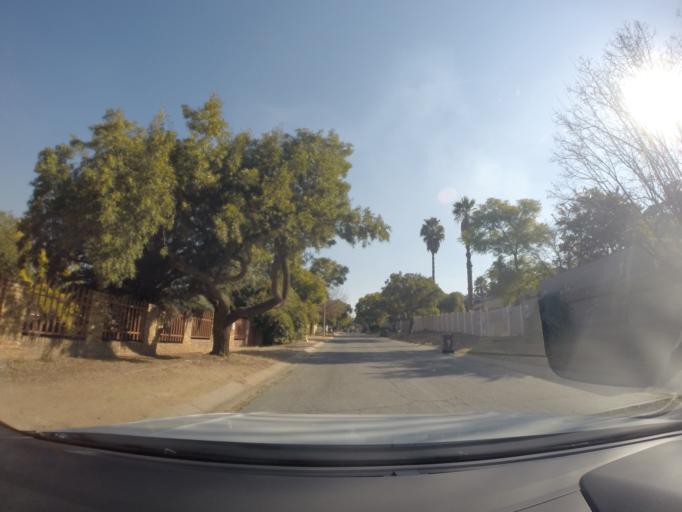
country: ZA
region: Gauteng
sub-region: City of Johannesburg Metropolitan Municipality
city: Roodepoort
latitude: -26.1192
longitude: 27.9368
